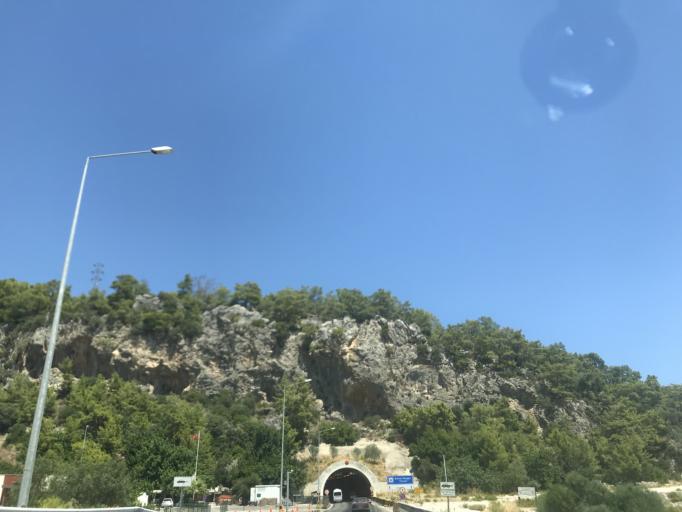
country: TR
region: Antalya
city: Cakirlar
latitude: 36.7613
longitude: 30.5698
